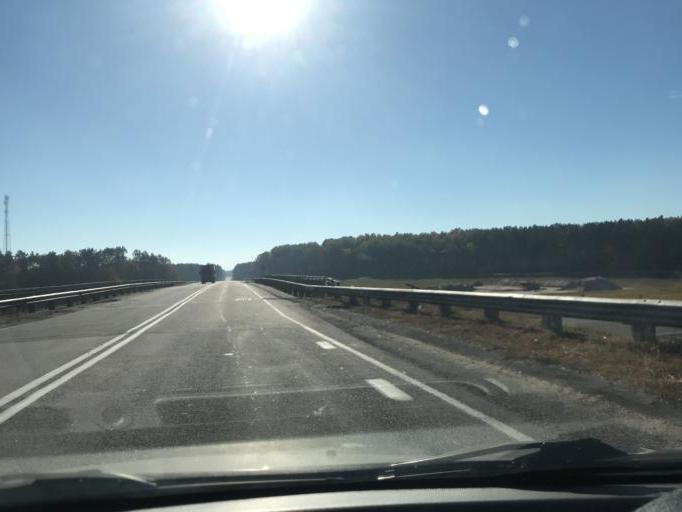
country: BY
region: Gomel
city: Gomel
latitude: 52.3882
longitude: 30.8279
